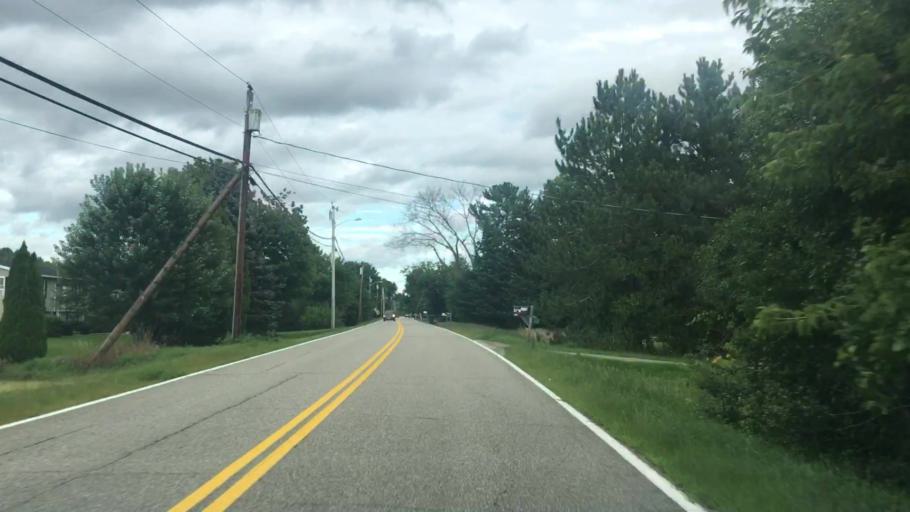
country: US
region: Maine
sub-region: York County
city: Biddeford
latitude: 43.5022
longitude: -70.4975
